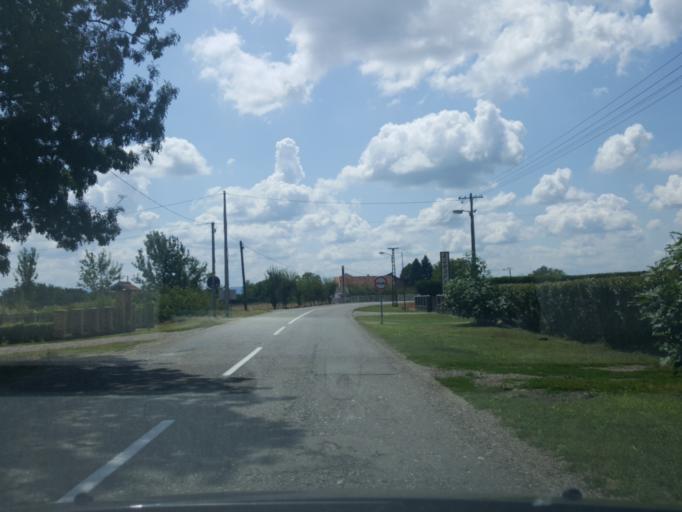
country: RS
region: Central Serbia
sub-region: Macvanski Okrug
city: Bogatic
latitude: 44.8162
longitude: 19.4775
